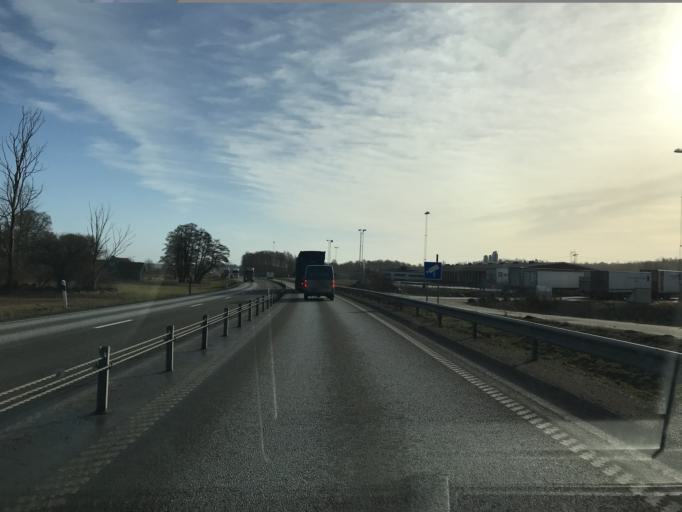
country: SE
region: Skane
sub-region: Kristianstads Kommun
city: Onnestad
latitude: 56.0402
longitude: 14.0346
